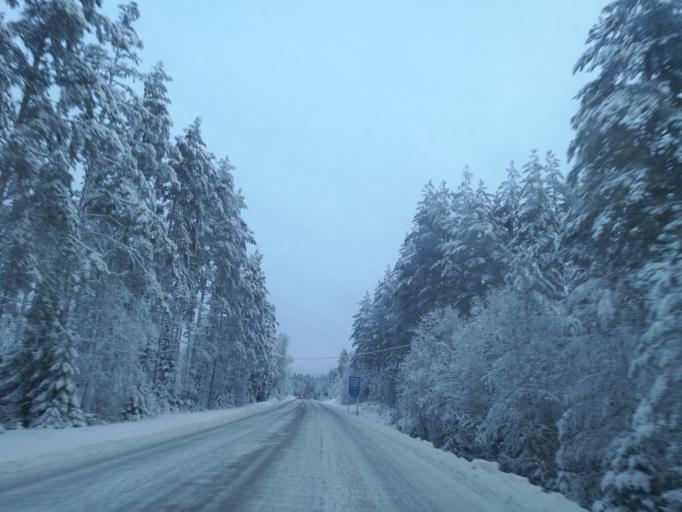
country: NO
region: Hedmark
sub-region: Grue
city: Kirkenaer
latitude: 60.4103
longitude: 12.3910
